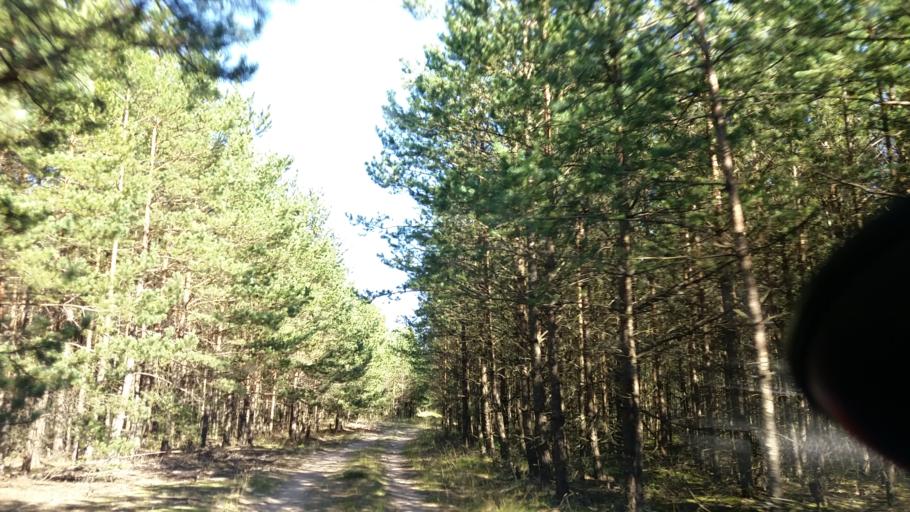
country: PL
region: West Pomeranian Voivodeship
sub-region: Powiat szczecinecki
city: Borne Sulinowo
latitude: 53.5789
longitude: 16.5154
